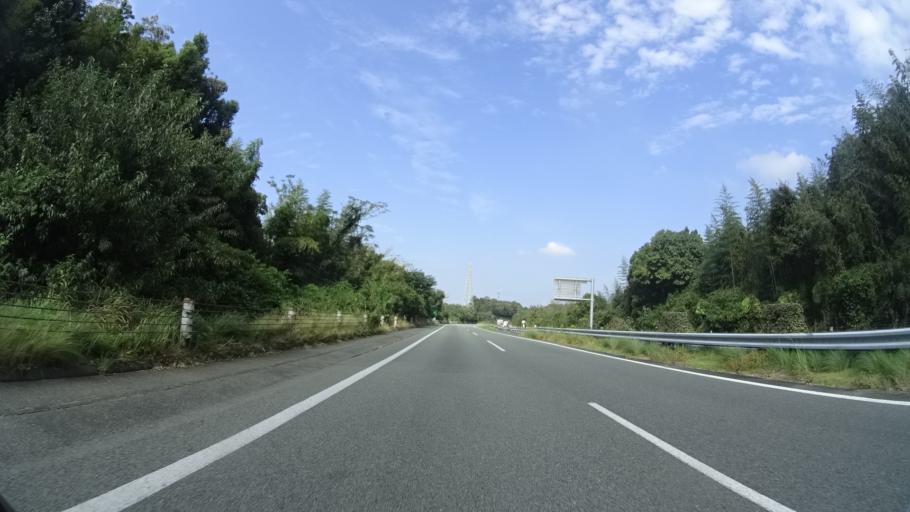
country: JP
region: Kumamoto
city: Matsubase
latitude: 32.6277
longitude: 130.7118
